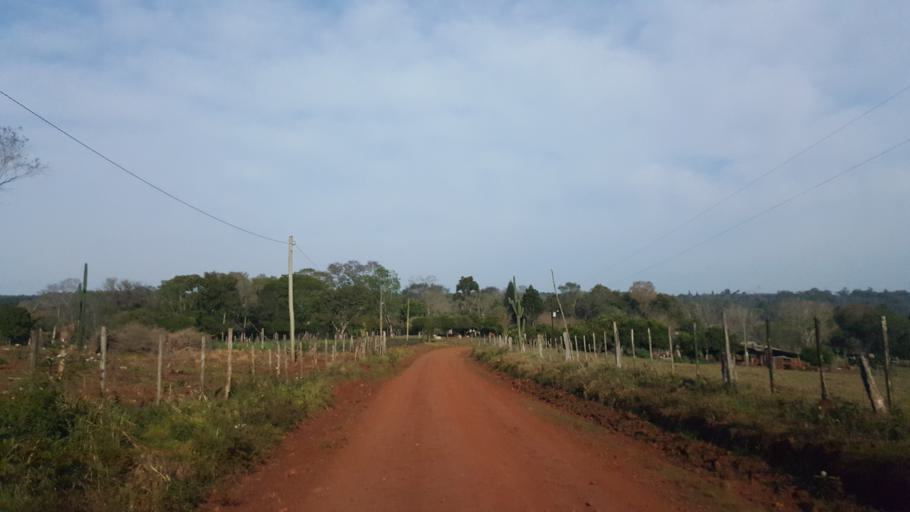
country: AR
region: Misiones
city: Capiovi
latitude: -26.9153
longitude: -55.0768
